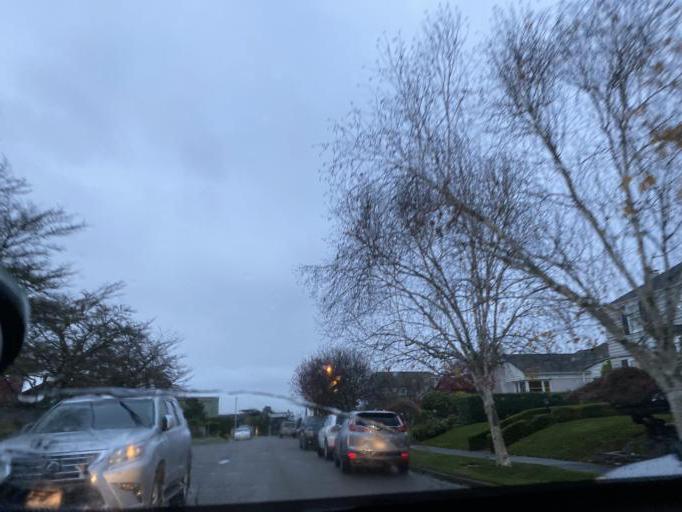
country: US
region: Washington
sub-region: King County
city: Seattle
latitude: 47.6417
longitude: -122.4067
